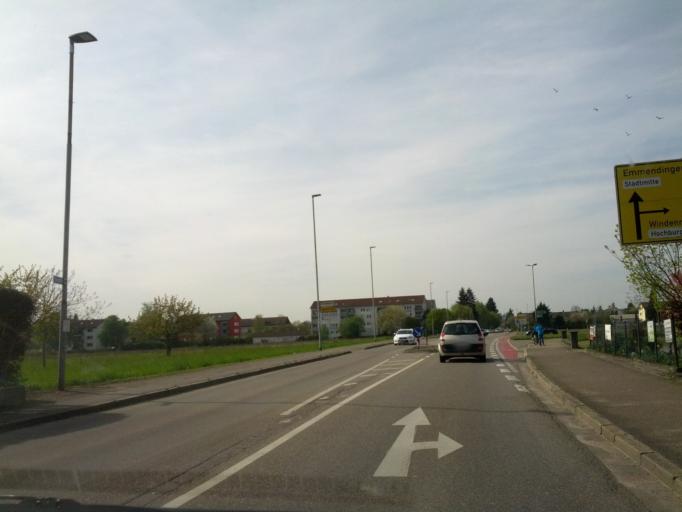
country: DE
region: Baden-Wuerttemberg
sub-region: Freiburg Region
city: Emmendingen
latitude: 48.1053
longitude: 7.8743
